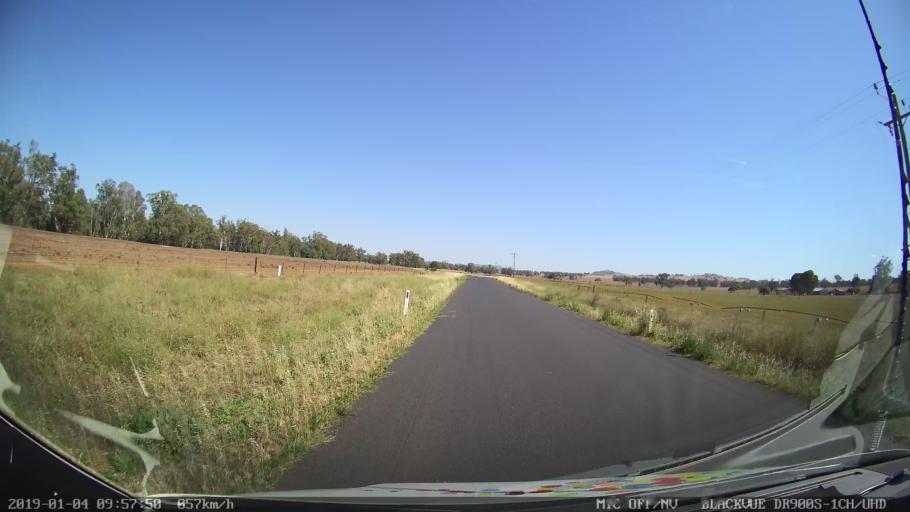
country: AU
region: New South Wales
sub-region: Cabonne
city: Canowindra
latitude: -33.5245
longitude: 148.3981
